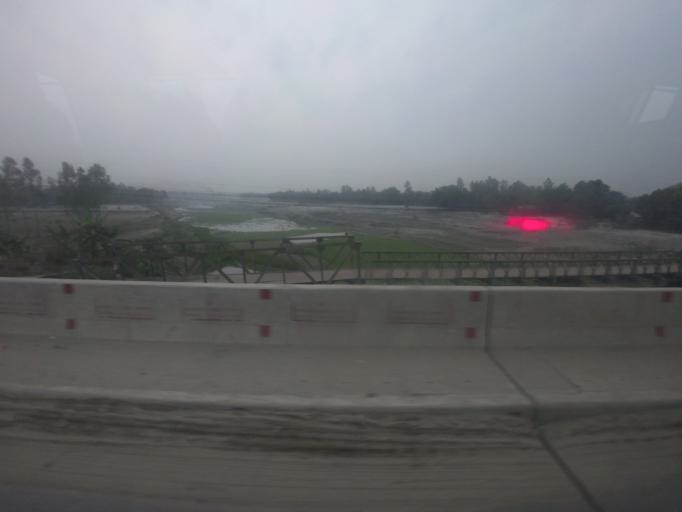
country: BD
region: Dhaka
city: Tangail
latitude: 24.3156
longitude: 89.9235
